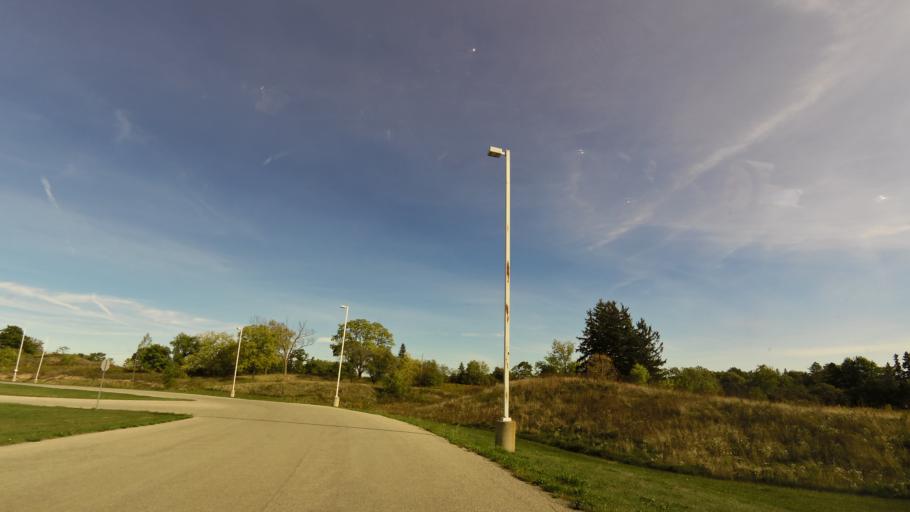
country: CA
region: Ontario
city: Ancaster
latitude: 43.0267
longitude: -79.9969
